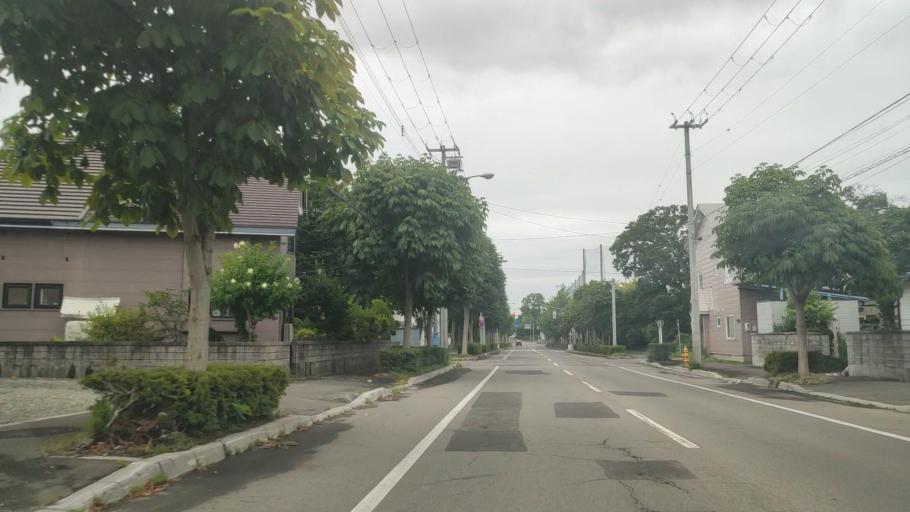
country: JP
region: Hokkaido
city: Hakodate
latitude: 41.7959
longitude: 140.7615
